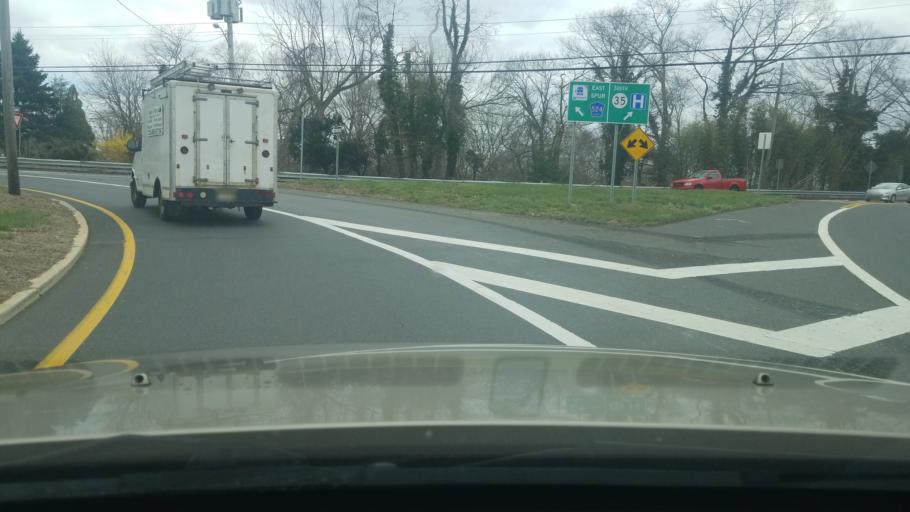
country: US
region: New Jersey
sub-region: Monmouth County
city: Manasquan
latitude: 40.1320
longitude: -74.0658
